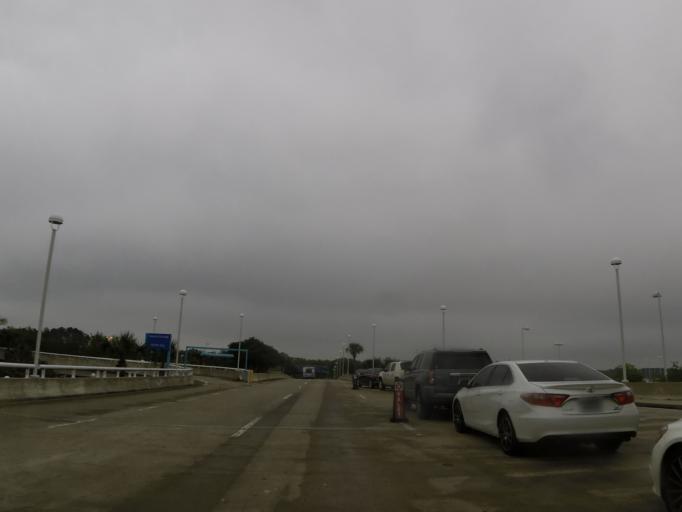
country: US
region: Florida
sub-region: Nassau County
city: Nassau Village-Ratliff
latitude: 30.4903
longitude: -81.6827
